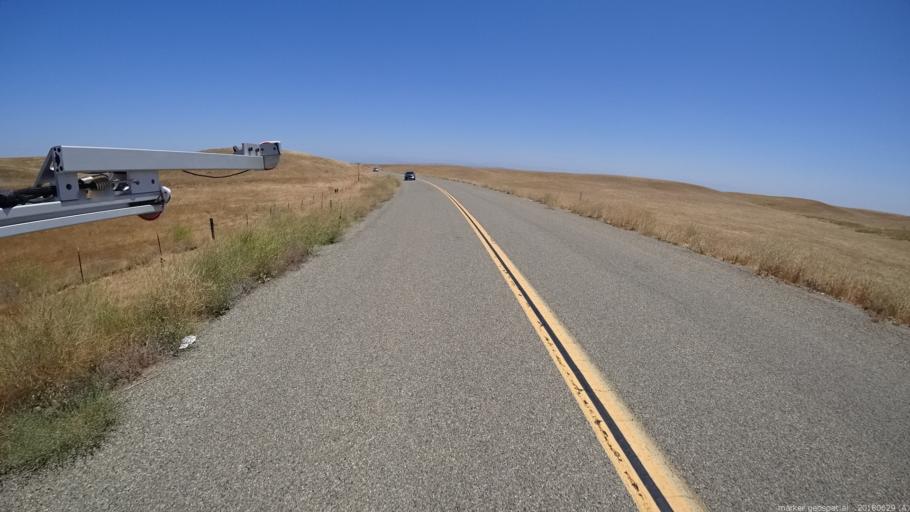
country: US
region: California
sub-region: Madera County
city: Bonadelle Ranchos-Madera Ranchos
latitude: 37.0259
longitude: -119.9438
